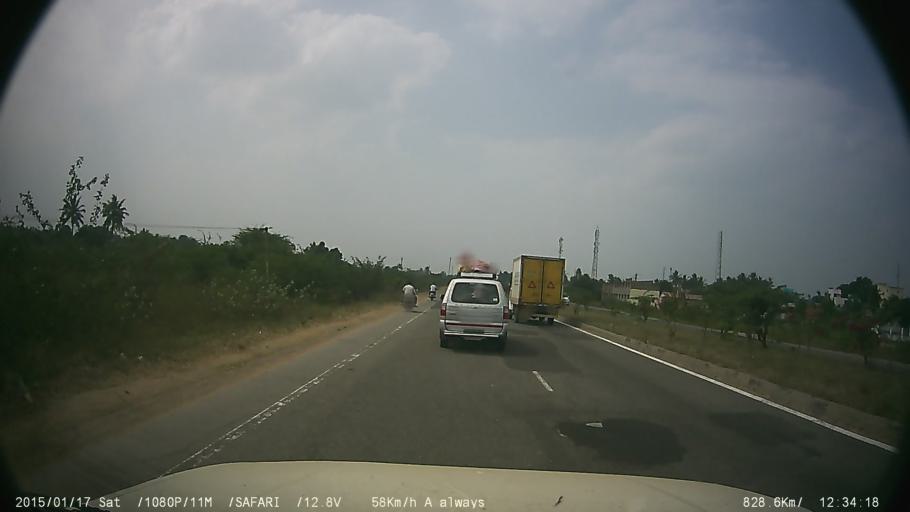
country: IN
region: Tamil Nadu
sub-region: Kancheepuram
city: Kanchipuram
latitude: 12.8745
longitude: 79.6245
